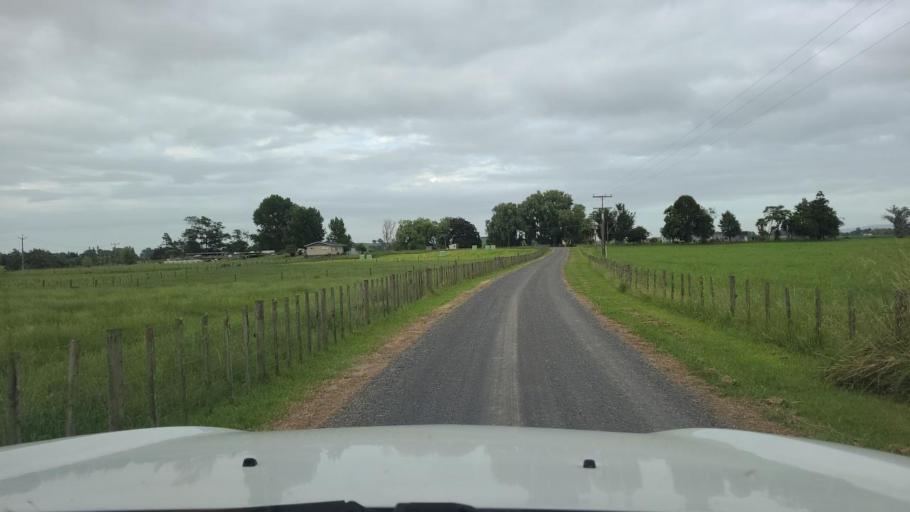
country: NZ
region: Waikato
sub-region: Hauraki District
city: Paeroa
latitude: -37.5723
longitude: 175.6665
